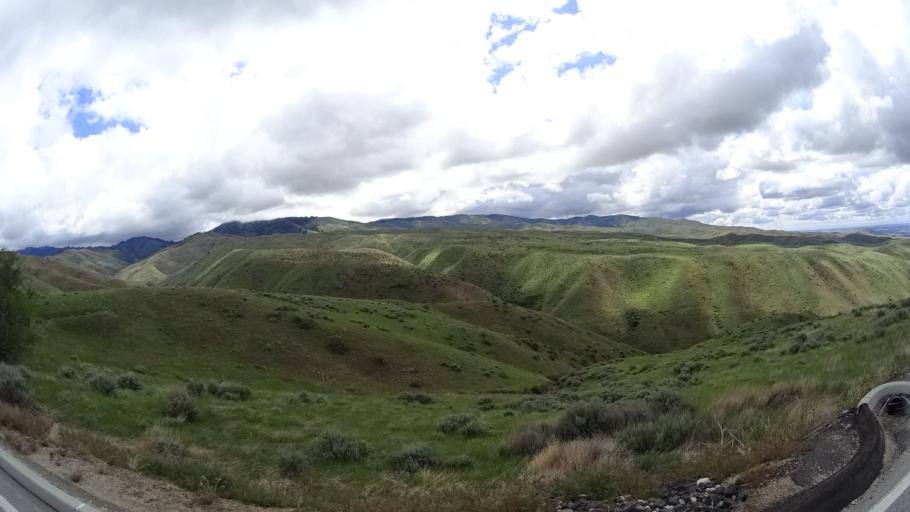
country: US
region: Idaho
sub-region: Ada County
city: Boise
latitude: 43.7000
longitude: -116.1648
